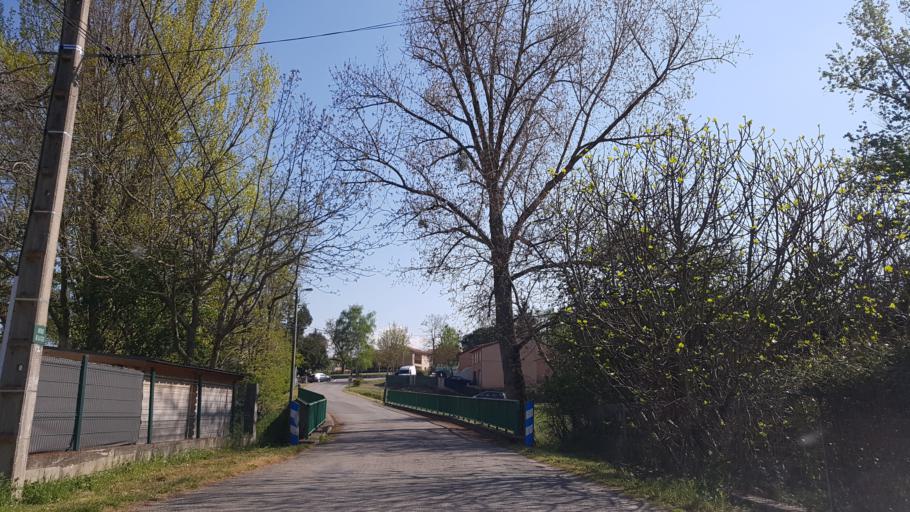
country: FR
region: Midi-Pyrenees
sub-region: Departement de l'Ariege
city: La Tour-du-Crieu
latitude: 43.0911
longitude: 1.7206
